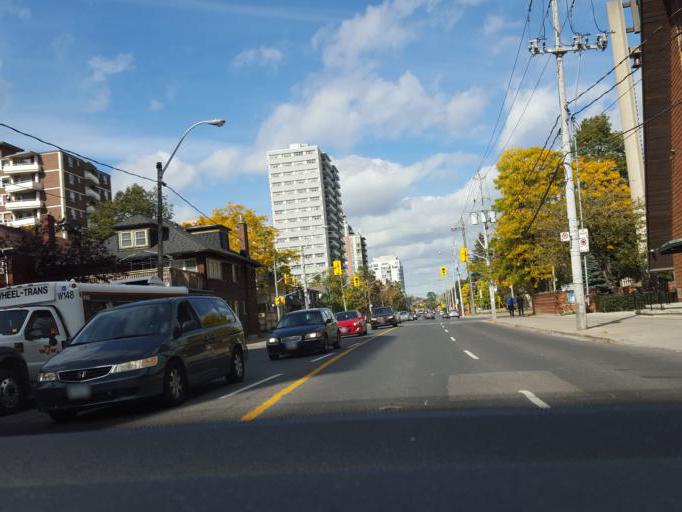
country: CA
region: Ontario
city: Toronto
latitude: 43.7089
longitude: -79.3904
